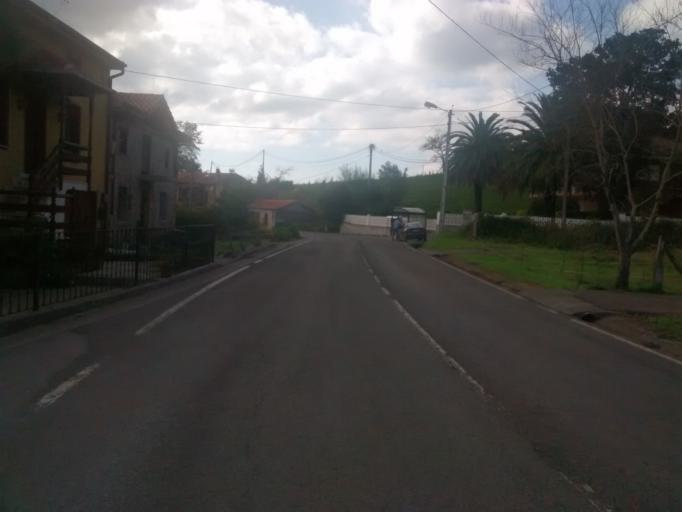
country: ES
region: Cantabria
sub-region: Provincia de Cantabria
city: Entrambasaguas
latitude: 43.3395
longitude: -3.6639
